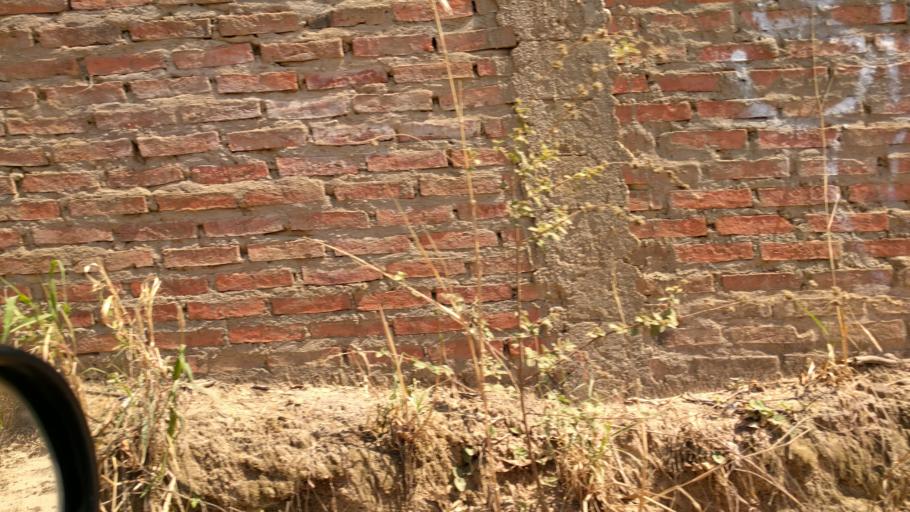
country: BO
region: Santa Cruz
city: Santa Cruz de la Sierra
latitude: -17.7554
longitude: -63.2312
